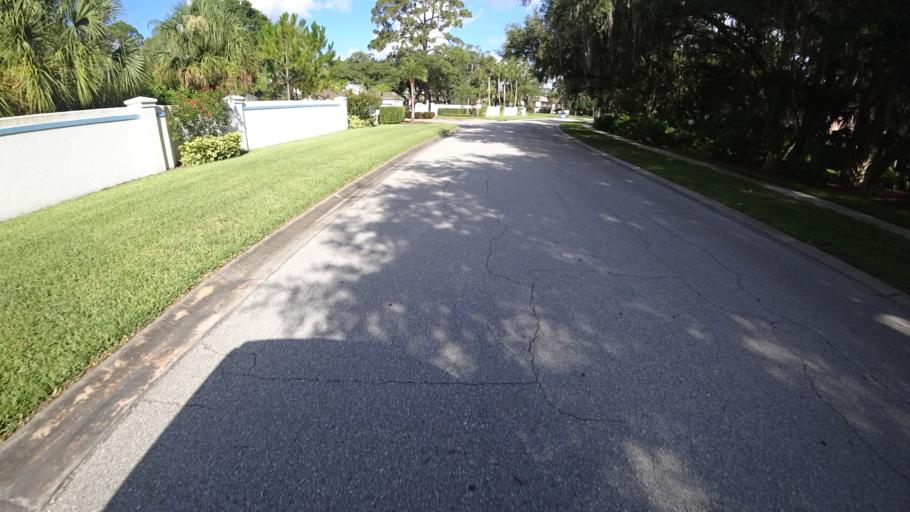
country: US
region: Florida
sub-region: Sarasota County
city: Desoto Lakes
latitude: 27.4006
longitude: -82.4823
